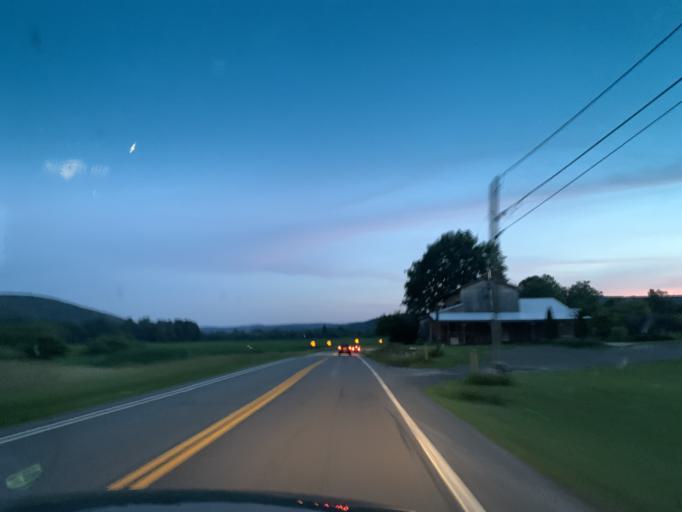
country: US
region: New York
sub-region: Chenango County
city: New Berlin
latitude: 42.5225
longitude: -75.3896
